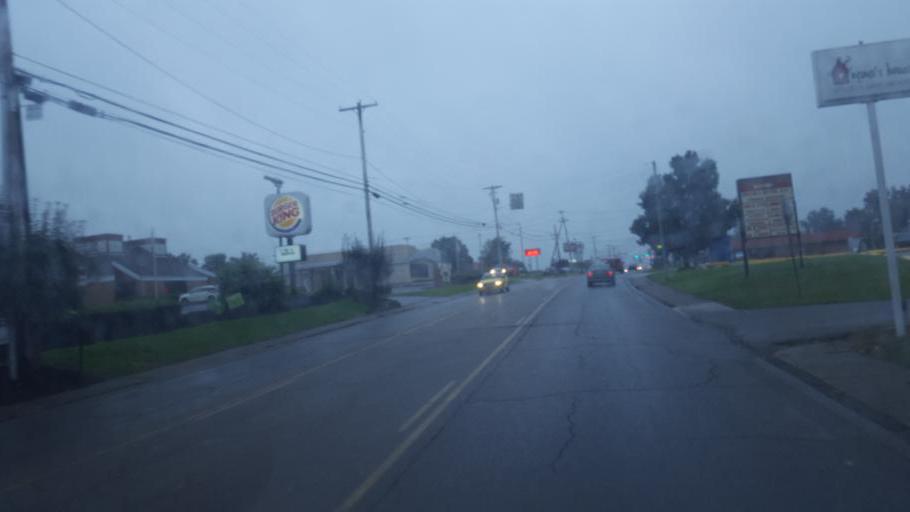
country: US
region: Ohio
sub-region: Jackson County
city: Jackson
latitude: 39.0430
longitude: -82.6292
